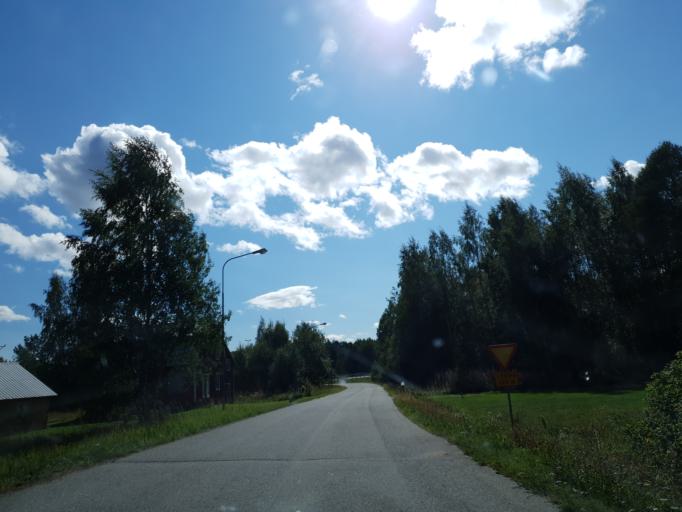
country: SE
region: Vaesternorrland
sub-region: OErnskoeldsviks Kommun
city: Husum
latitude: 63.3436
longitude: 19.1137
